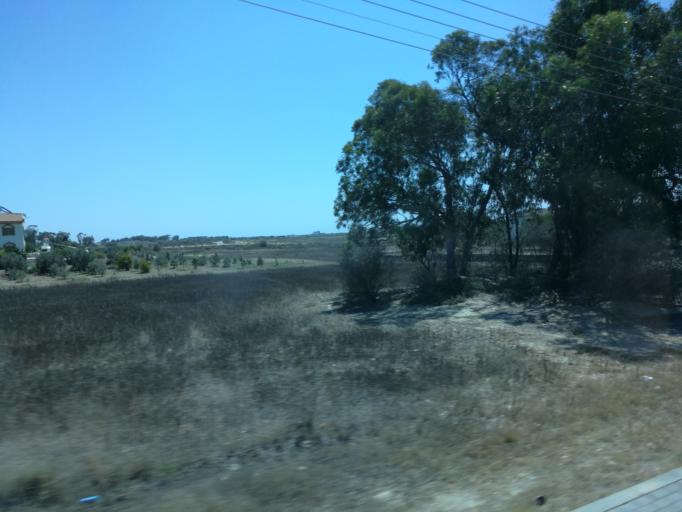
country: CY
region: Ammochostos
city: Famagusta
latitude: 35.1612
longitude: 33.9017
